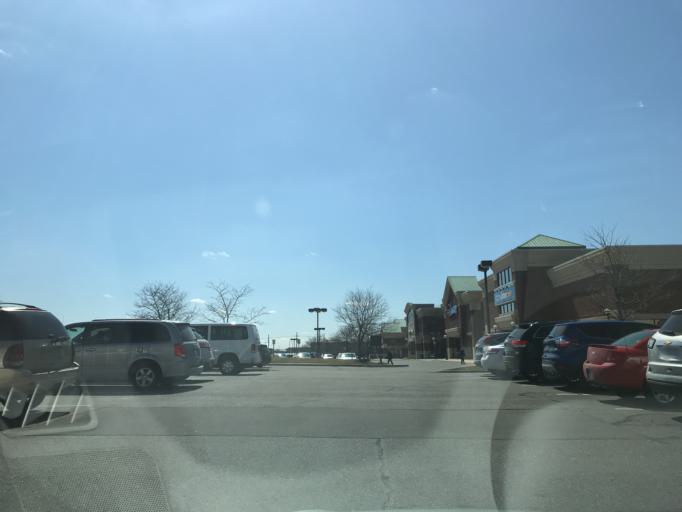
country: US
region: Michigan
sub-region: Oakland County
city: West Bloomfield Township
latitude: 42.5314
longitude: -83.3626
